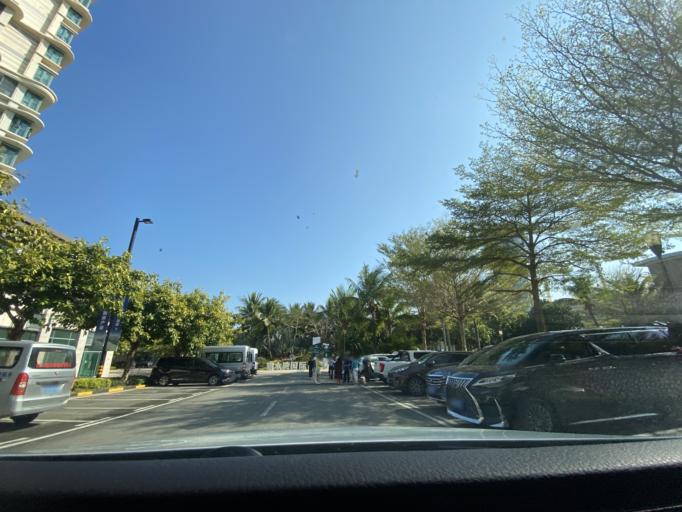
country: CN
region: Hainan
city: Yingzhou
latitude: 18.4087
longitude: 109.8755
